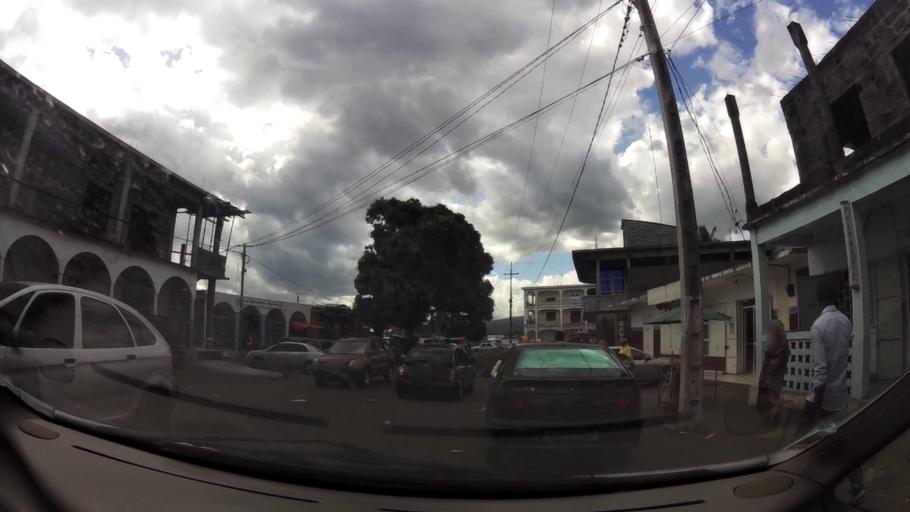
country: KM
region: Grande Comore
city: Tsidje
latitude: -11.6904
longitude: 43.2570
